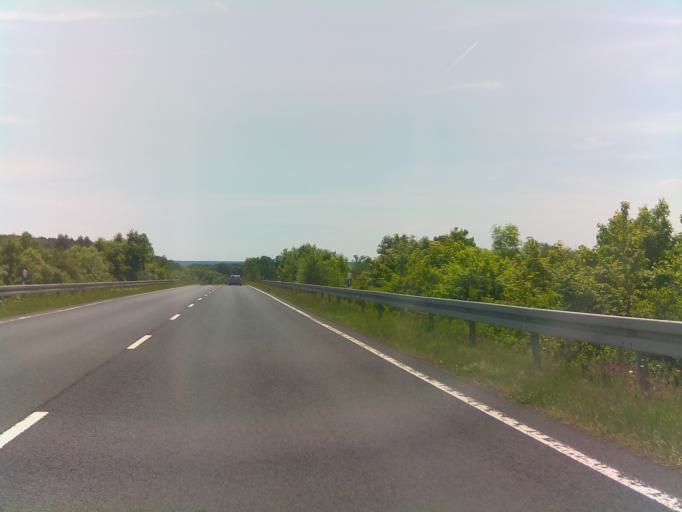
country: DE
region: Bavaria
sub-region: Regierungsbezirk Unterfranken
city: Oerlenbach
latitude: 50.1735
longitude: 10.1524
